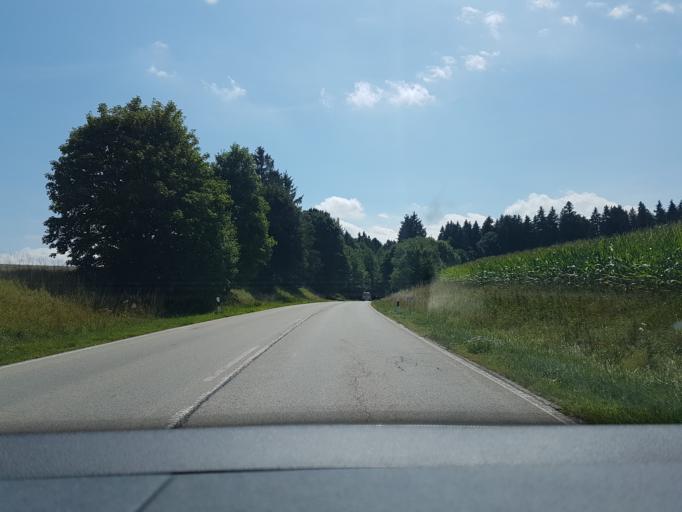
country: DE
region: Bavaria
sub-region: Upper Bavaria
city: Miesbach
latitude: 47.8189
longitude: 11.8372
